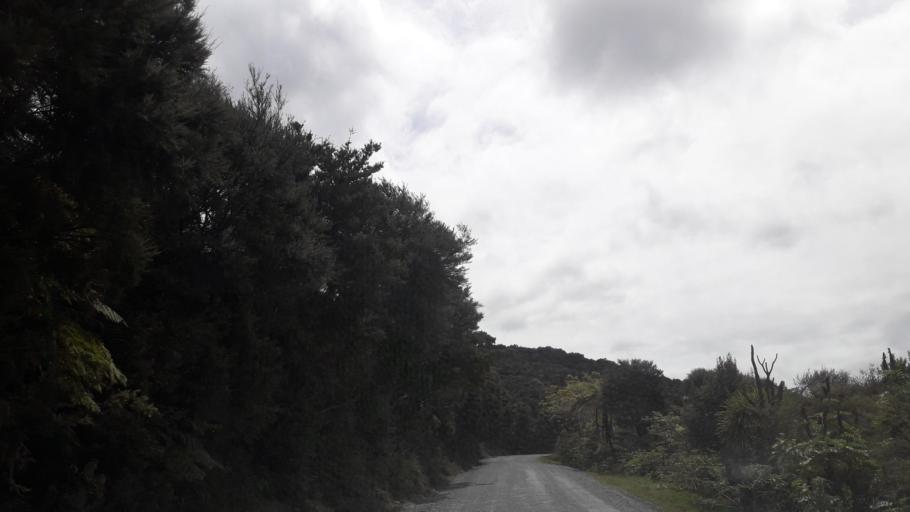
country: NZ
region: Northland
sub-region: Far North District
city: Taipa
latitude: -35.0332
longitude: 173.5639
